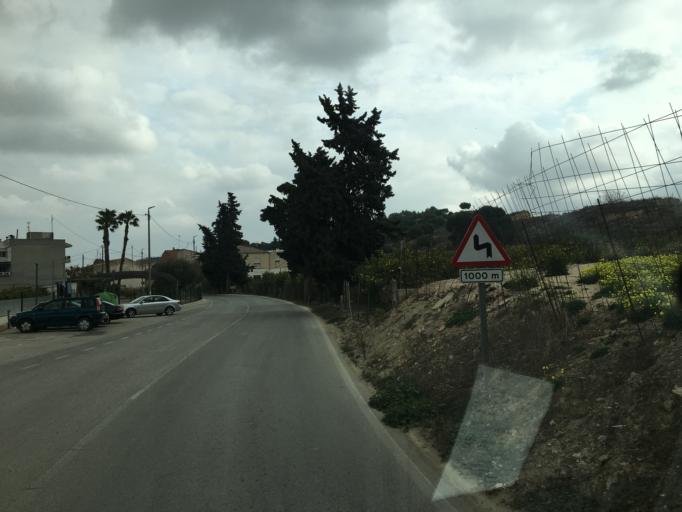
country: ES
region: Murcia
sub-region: Murcia
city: Beniel
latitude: 38.0140
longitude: -0.9918
